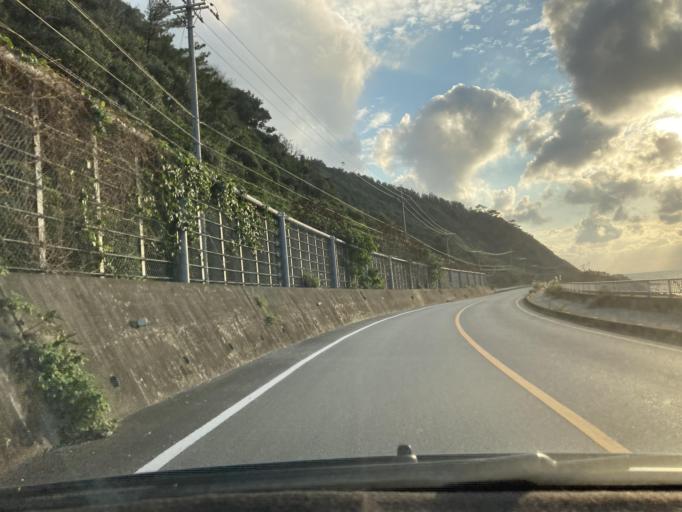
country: JP
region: Okinawa
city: Nago
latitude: 26.8230
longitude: 128.2430
